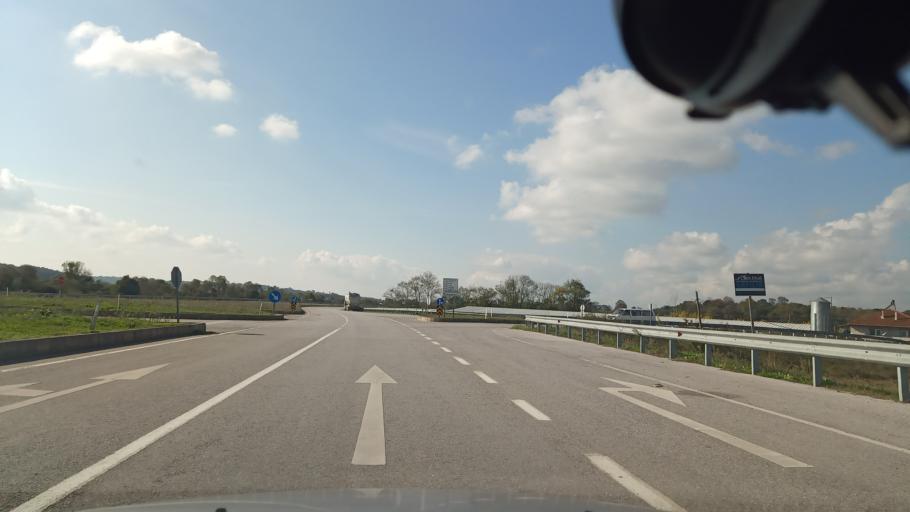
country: TR
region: Sakarya
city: Kaynarca
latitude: 41.0745
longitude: 30.4003
